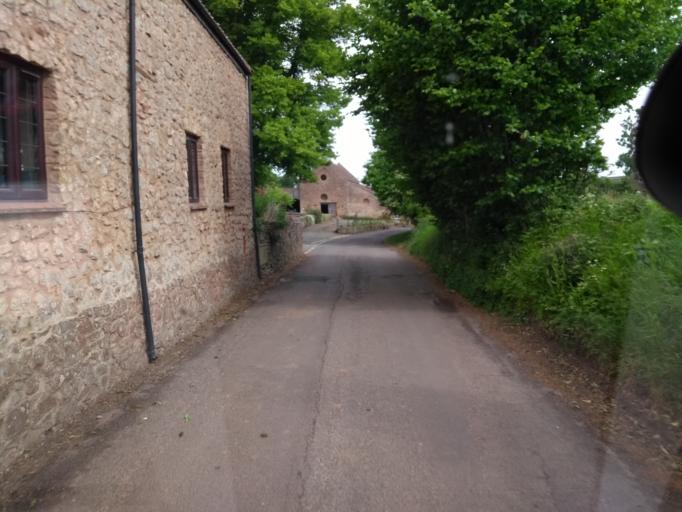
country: GB
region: England
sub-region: Somerset
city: North Petherton
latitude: 51.1269
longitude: -3.1076
